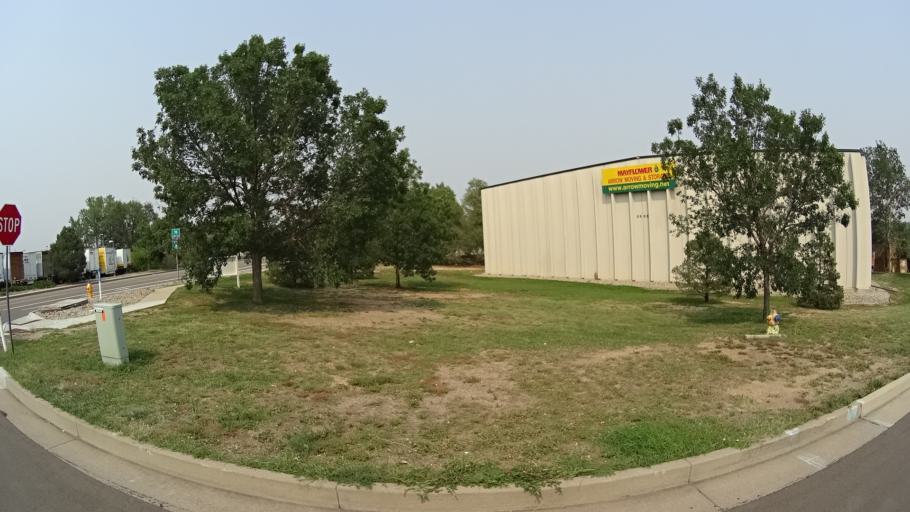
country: US
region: Colorado
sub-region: El Paso County
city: Stratmoor
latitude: 38.7898
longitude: -104.7900
